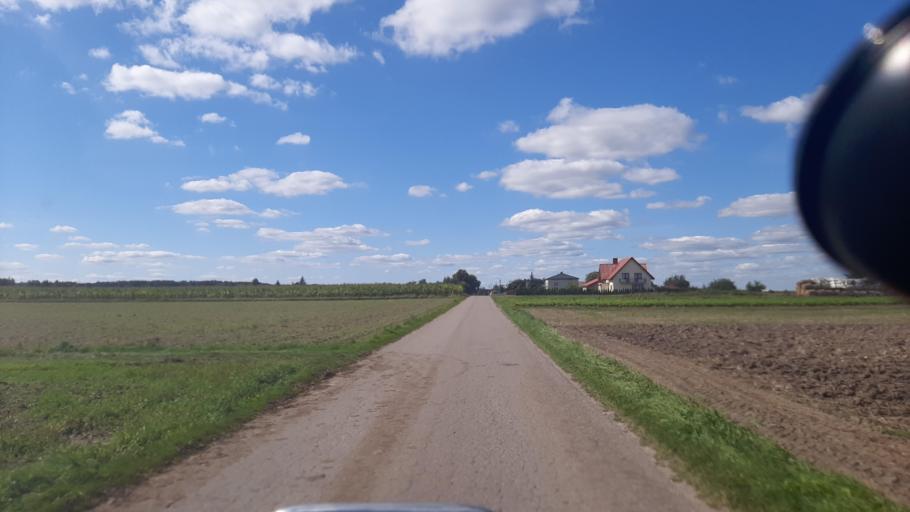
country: PL
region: Lublin Voivodeship
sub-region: Powiat lubartowski
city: Kamionka
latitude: 51.4053
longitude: 22.4060
